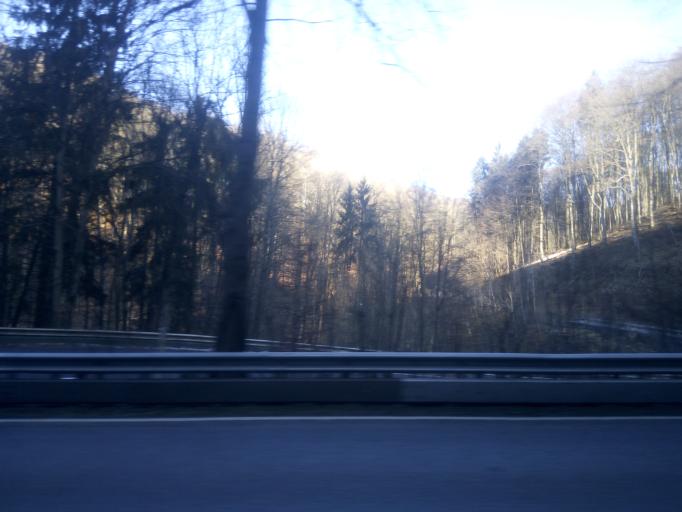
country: LU
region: Luxembourg
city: Helmsange
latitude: 49.6453
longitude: 6.1665
